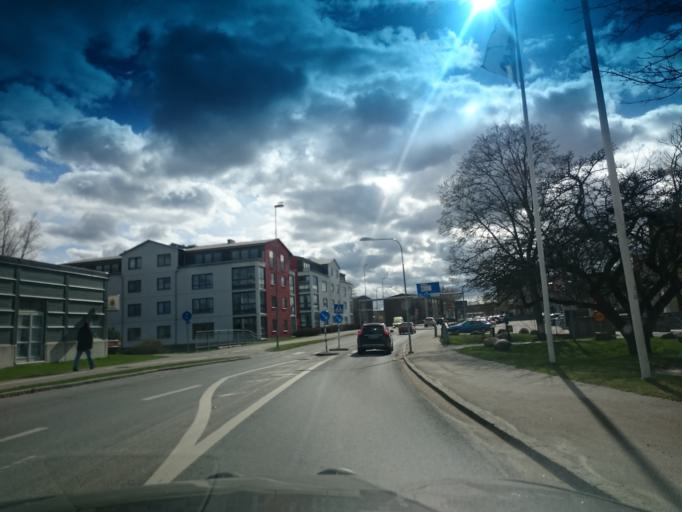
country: SE
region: Joenkoeping
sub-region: Vetlanda Kommun
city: Vetlanda
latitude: 57.4253
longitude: 15.0898
